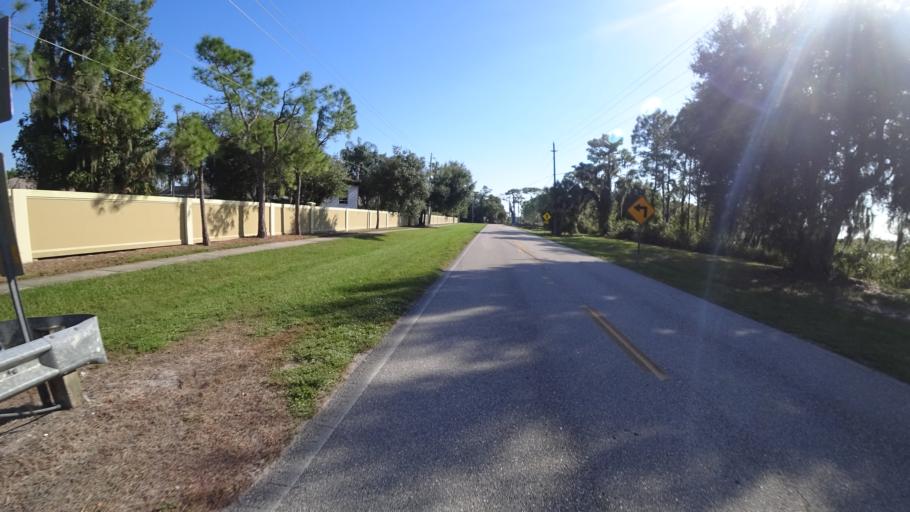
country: US
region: Florida
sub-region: Sarasota County
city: Desoto Lakes
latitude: 27.4339
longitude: -82.4811
